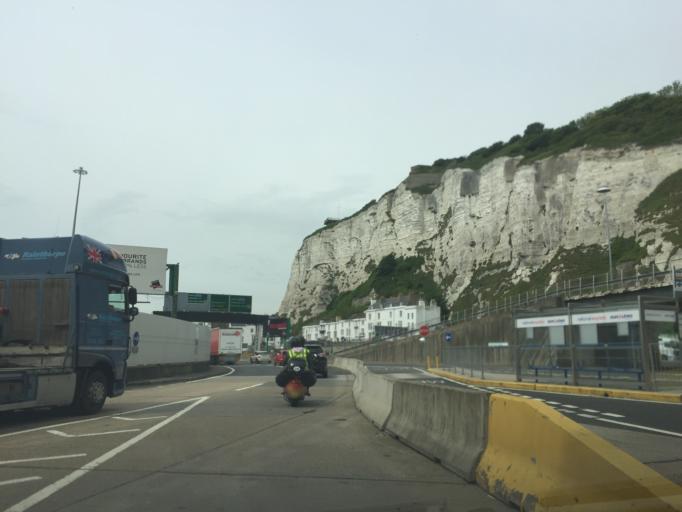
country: GB
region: England
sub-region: Kent
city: Dover
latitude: 51.1272
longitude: 1.3298
